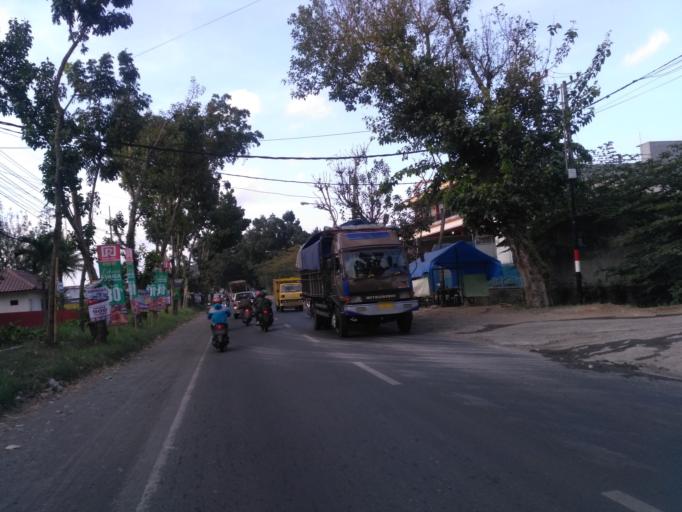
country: ID
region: East Java
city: Watudakon
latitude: -8.0384
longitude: 112.6104
